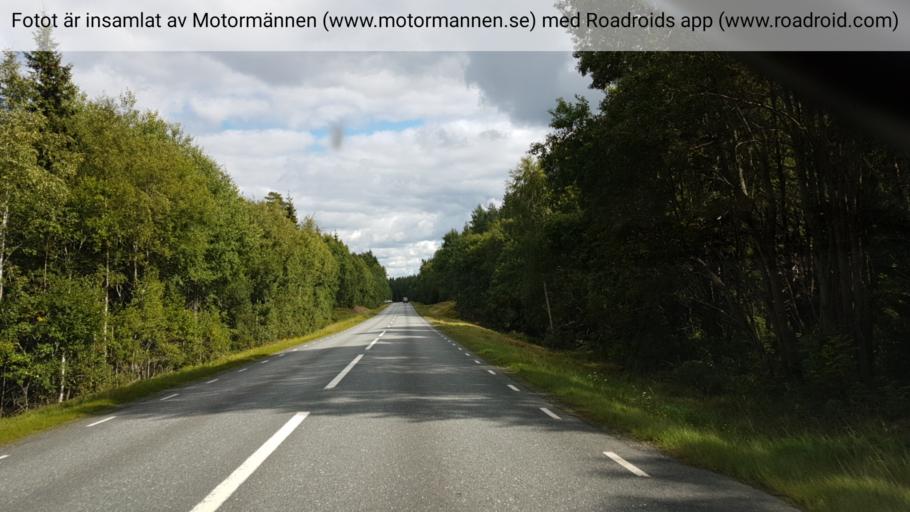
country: SE
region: Joenkoeping
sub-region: Aneby Kommun
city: Aneby
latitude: 57.8056
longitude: 14.7163
